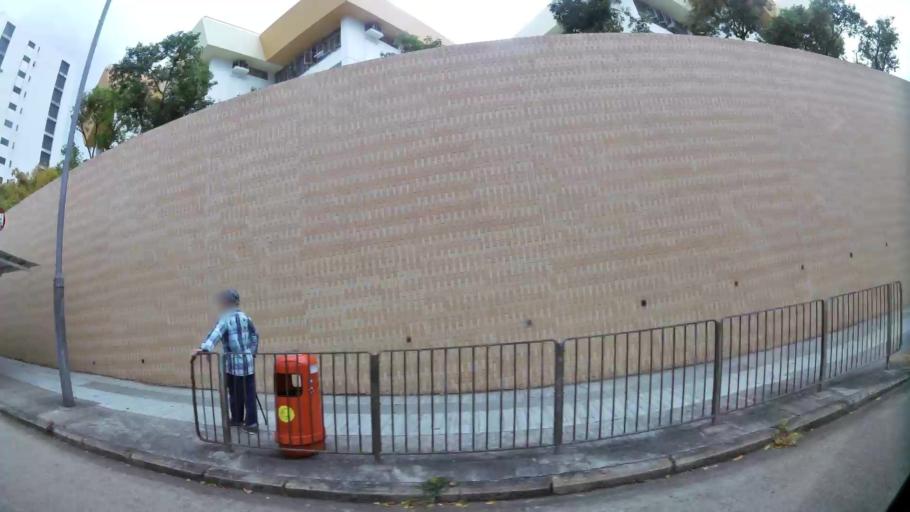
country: HK
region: Sham Shui Po
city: Sham Shui Po
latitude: 22.3386
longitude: 114.1676
